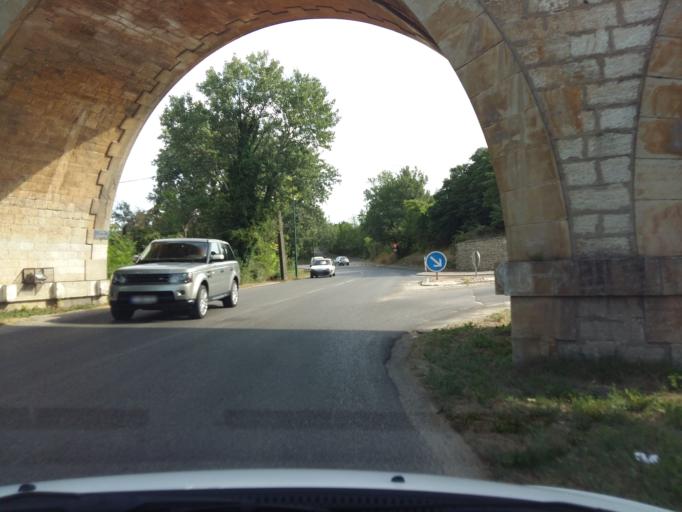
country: FR
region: Provence-Alpes-Cote d'Azur
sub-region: Departement du Vaucluse
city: Apt
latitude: 43.8852
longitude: 5.3808
